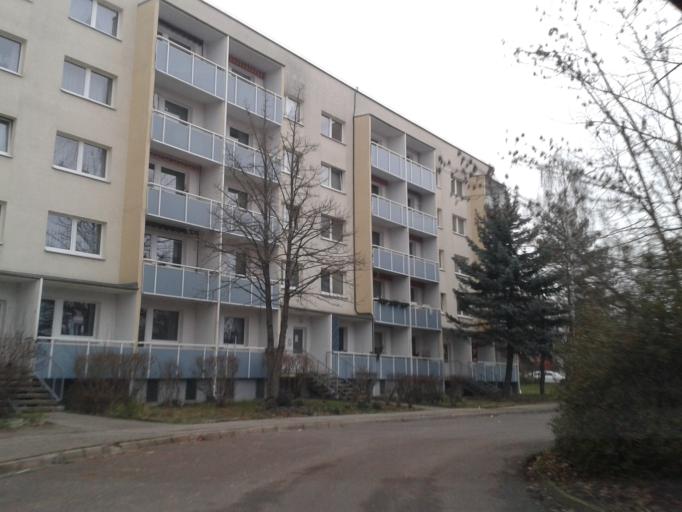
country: DE
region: Saxony-Anhalt
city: Halle Neustadt
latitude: 51.4497
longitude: 11.9595
